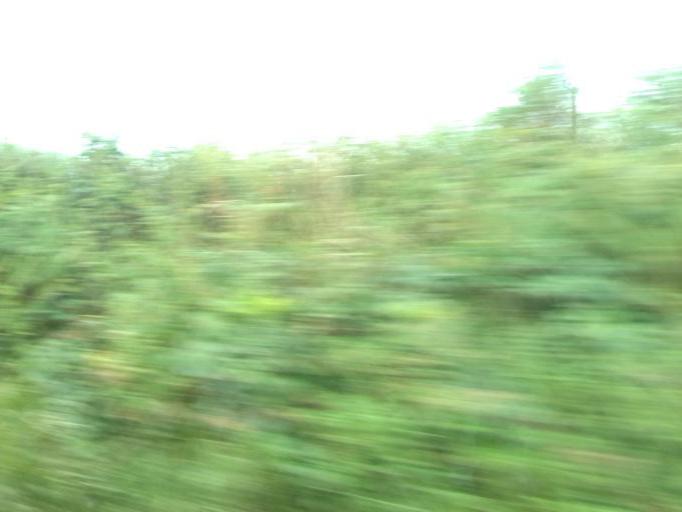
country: IE
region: Leinster
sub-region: Loch Garman
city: Ballinroad
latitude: 52.4897
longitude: -6.4707
